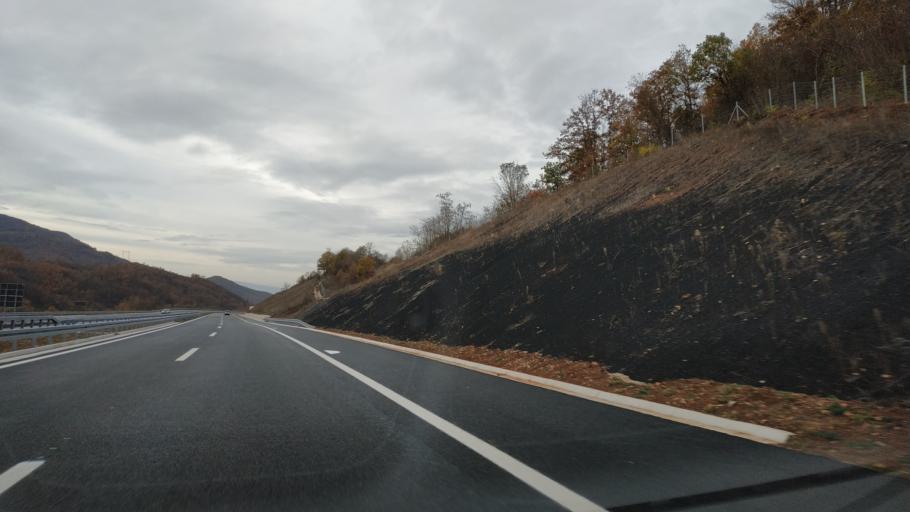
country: RS
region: Central Serbia
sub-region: Nisavski Okrug
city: Gadzin Han
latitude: 43.2817
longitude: 22.1322
